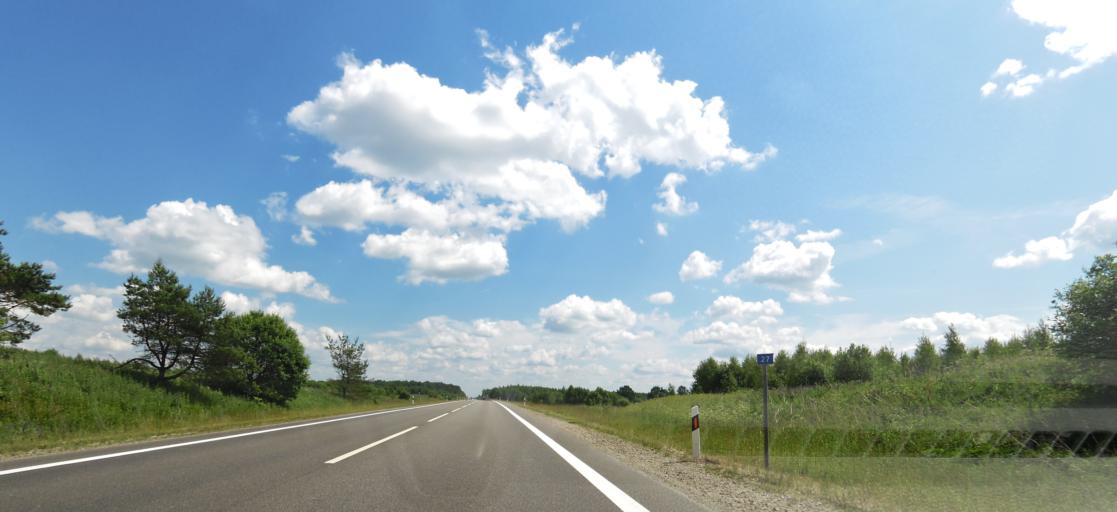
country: LT
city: Skaidiskes
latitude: 54.5750
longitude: 25.6082
